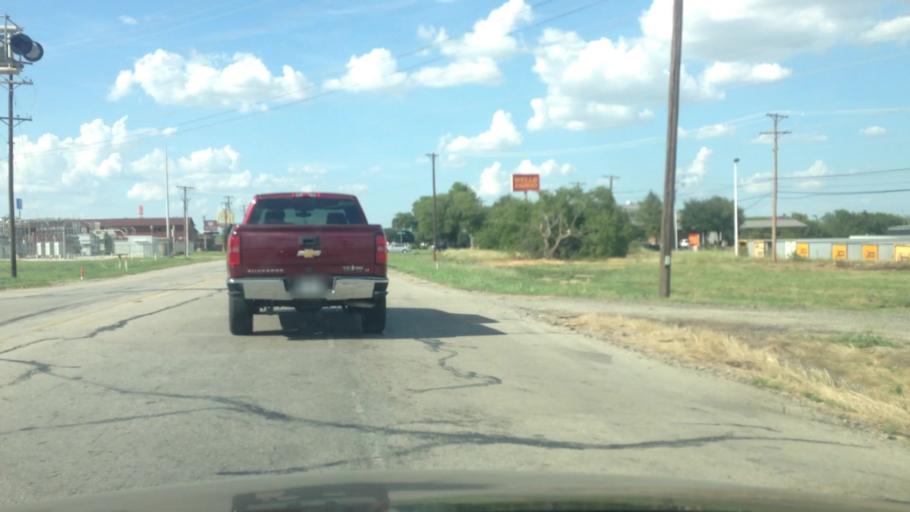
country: US
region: Texas
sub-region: Tarrant County
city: Blue Mound
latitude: 32.8374
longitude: -97.3430
